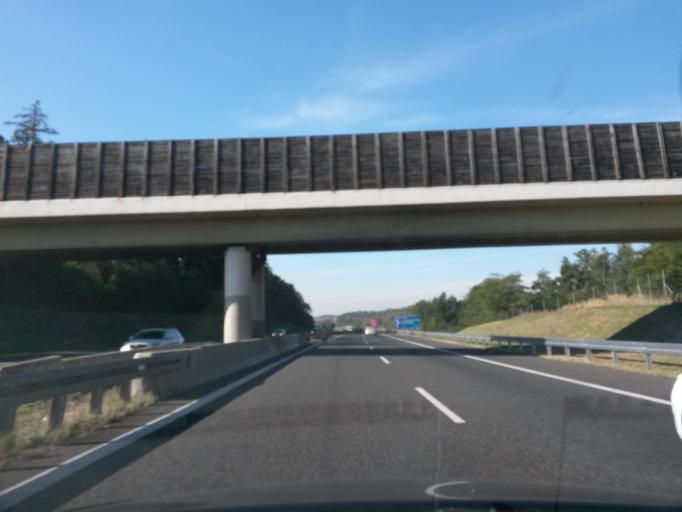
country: PL
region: Silesian Voivodeship
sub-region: Powiat gliwicki
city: Rudziniec
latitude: 50.3830
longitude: 18.4622
